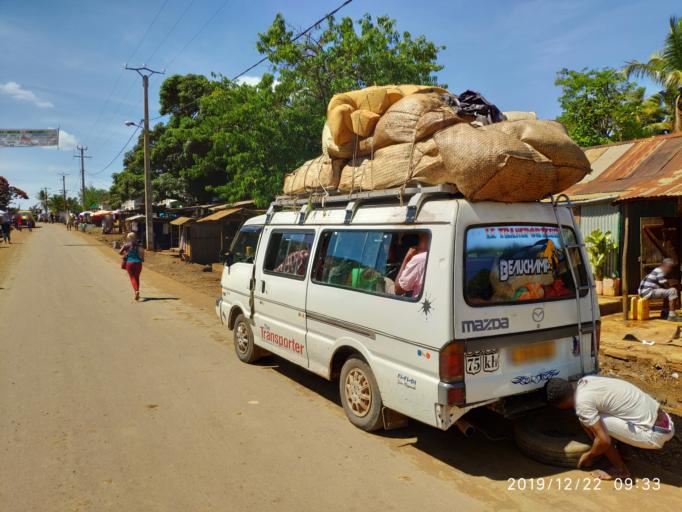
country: MG
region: Diana
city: Sadjoavato
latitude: -12.7406
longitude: 49.2336
